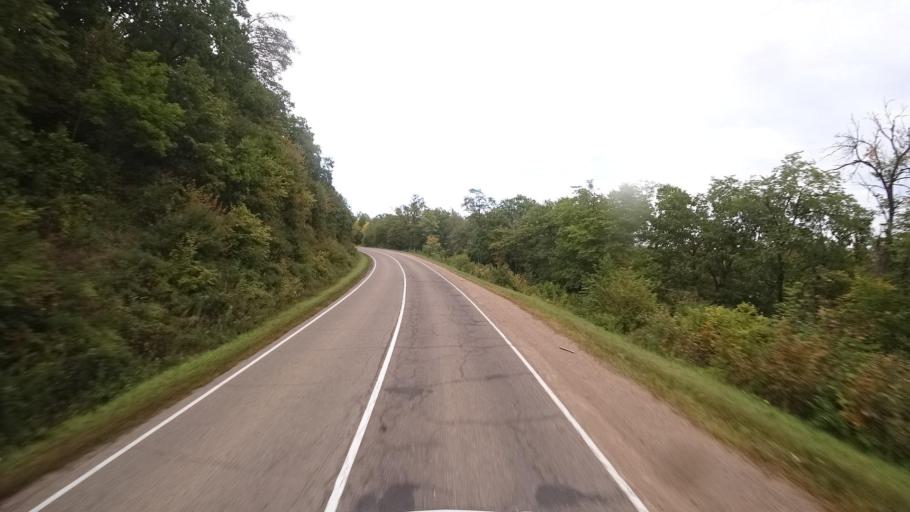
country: RU
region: Primorskiy
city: Yakovlevka
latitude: 44.3924
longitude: 133.4694
